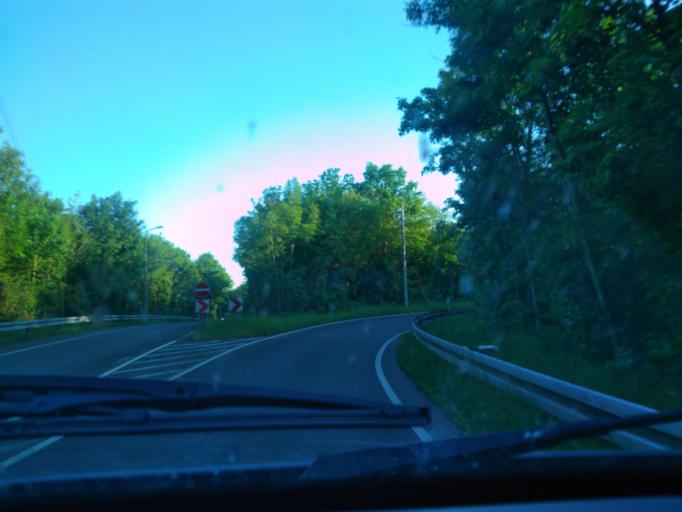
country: DE
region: Saxony
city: Markkleeberg
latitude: 51.3019
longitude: 12.3757
